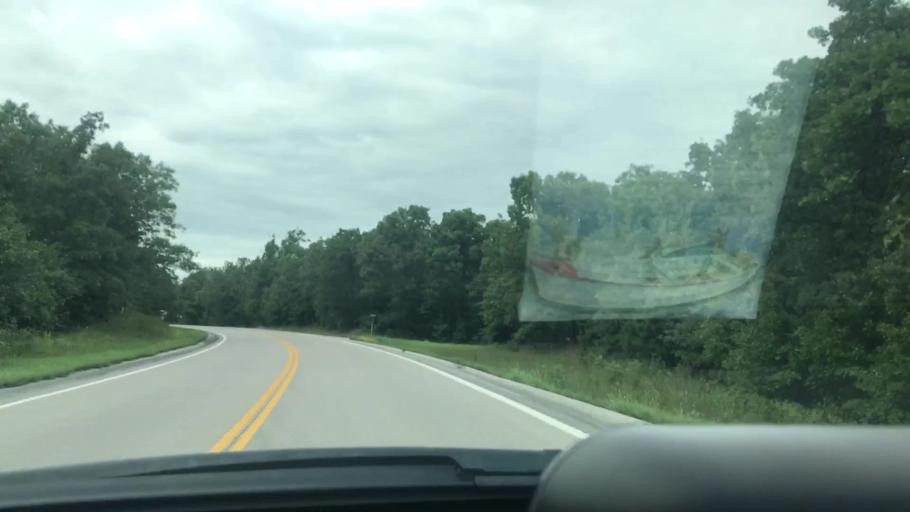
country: US
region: Missouri
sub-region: Benton County
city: Warsaw
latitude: 38.1602
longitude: -93.2981
